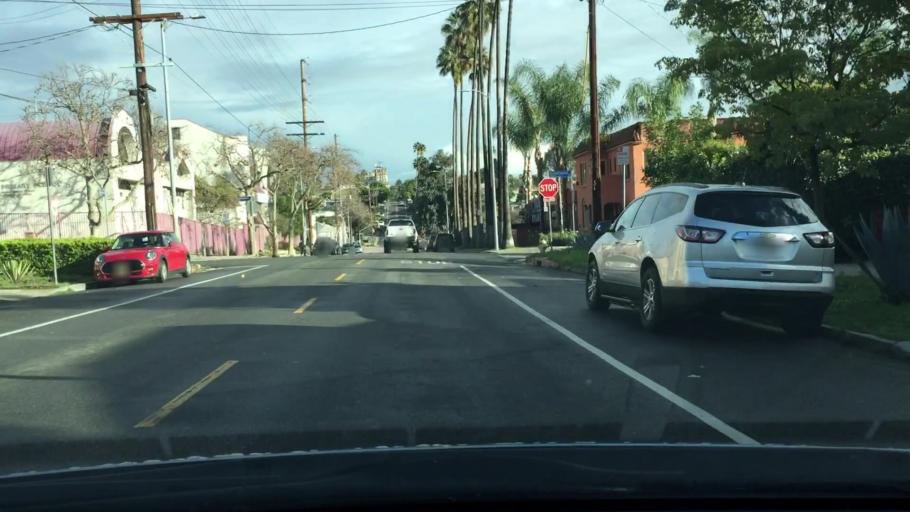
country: US
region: California
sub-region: Los Angeles County
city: Silver Lake
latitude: 34.0794
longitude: -118.2815
